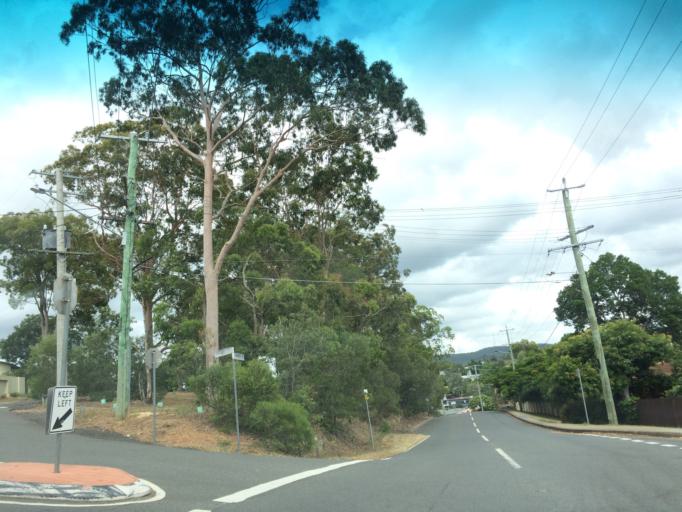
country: AU
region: Queensland
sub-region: Brisbane
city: Toowong
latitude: -27.4982
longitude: 153.0024
